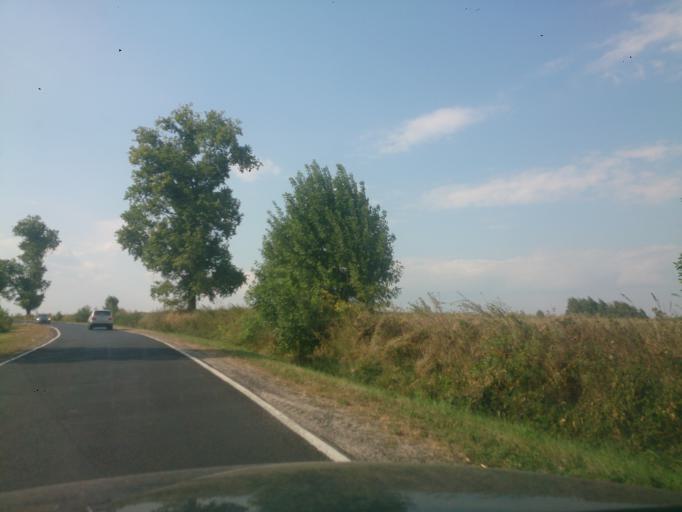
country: PL
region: Swietokrzyskie
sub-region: Powiat sandomierski
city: Klimontow
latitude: 50.6900
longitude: 21.3796
